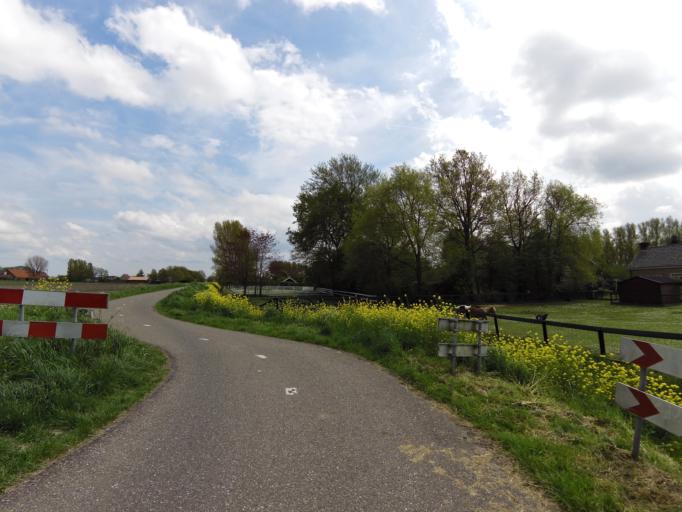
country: NL
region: South Holland
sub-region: Gemeente Hellevoetsluis
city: Nieuwenhoorn
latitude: 51.8313
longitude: 4.1881
